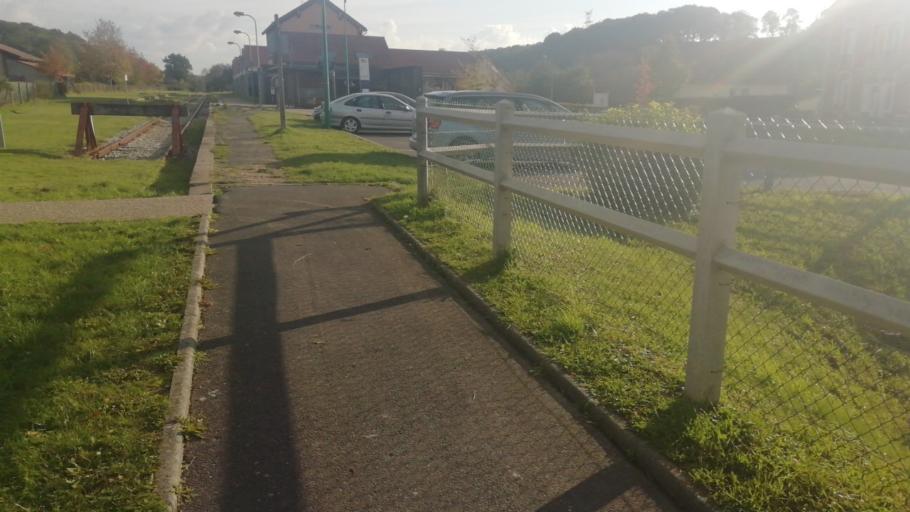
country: FR
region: Haute-Normandie
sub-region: Departement de la Seine-Maritime
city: Rolleville
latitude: 49.5824
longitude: 0.2157
